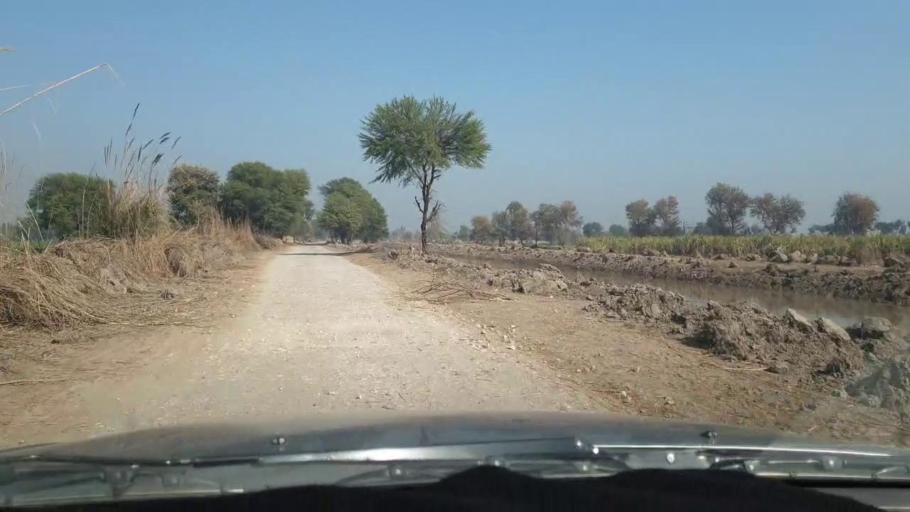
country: PK
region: Sindh
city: Khanpur
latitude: 27.7725
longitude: 69.5351
